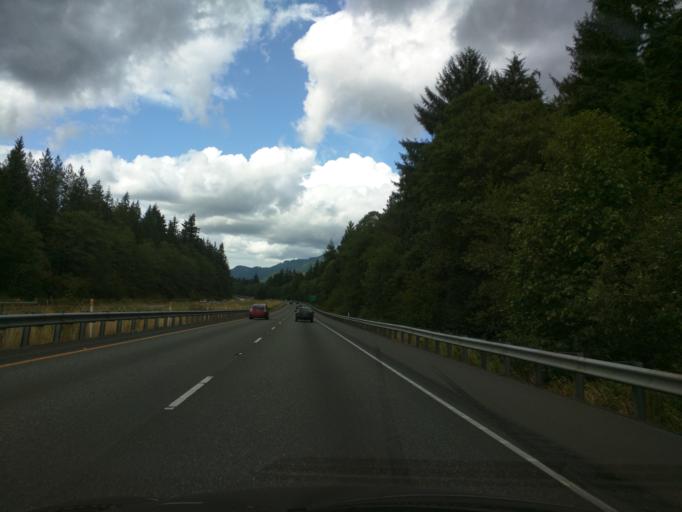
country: US
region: Washington
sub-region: Whatcom County
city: Sudden Valley
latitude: 48.6013
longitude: -122.3447
